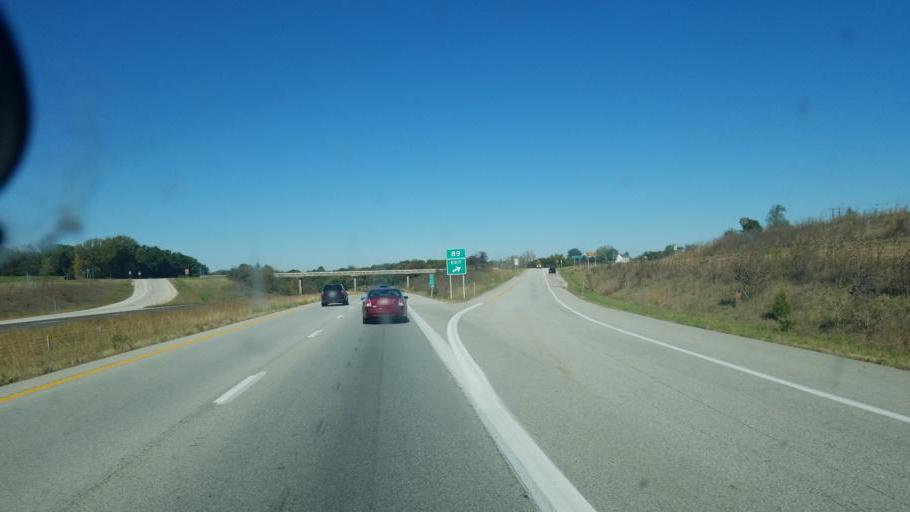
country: US
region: Missouri
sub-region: Cooper County
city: Boonville
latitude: 38.9430
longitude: -92.9886
